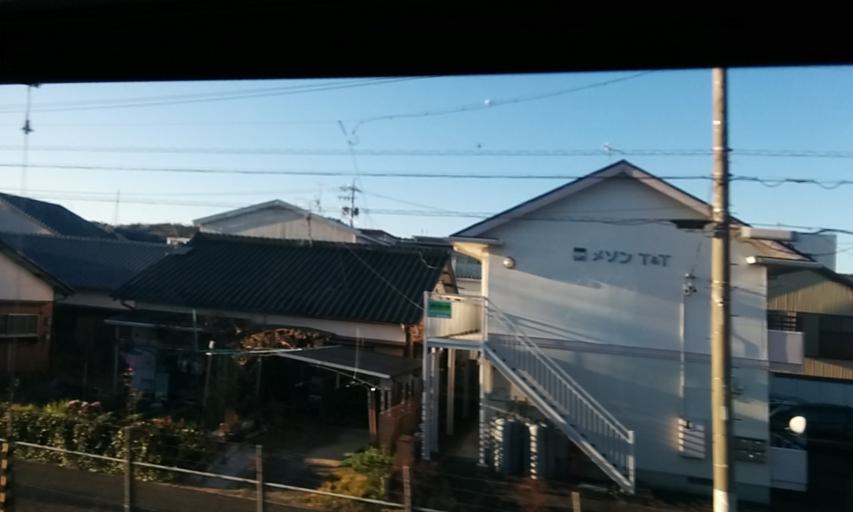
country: JP
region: Gifu
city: Toki
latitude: 35.3642
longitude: 137.1897
